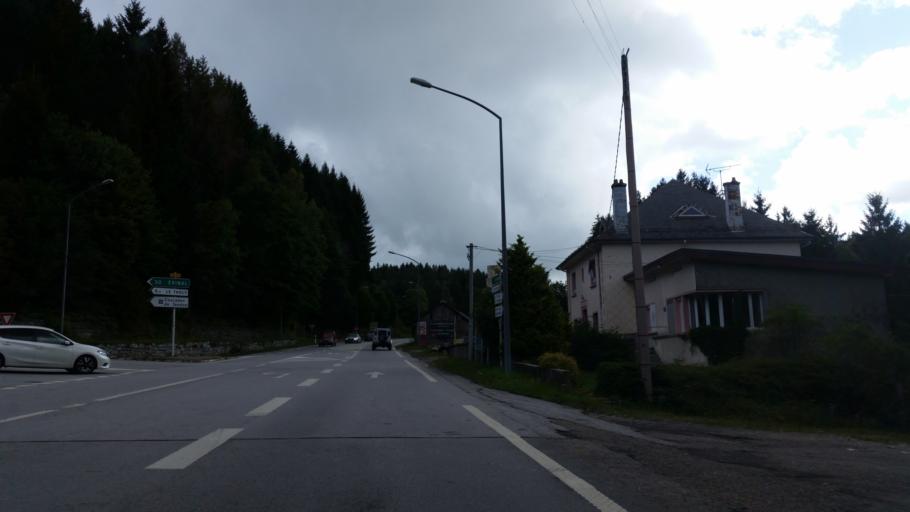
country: FR
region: Lorraine
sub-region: Departement des Vosges
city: Le Tholy
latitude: 48.0822
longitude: 6.7519
